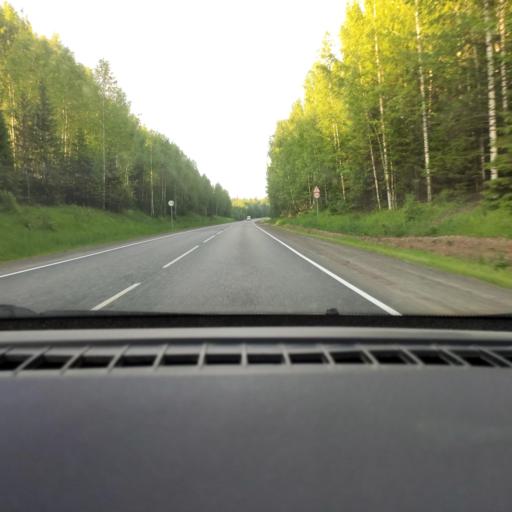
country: RU
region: Perm
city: Ocher
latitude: 57.8331
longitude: 54.6833
